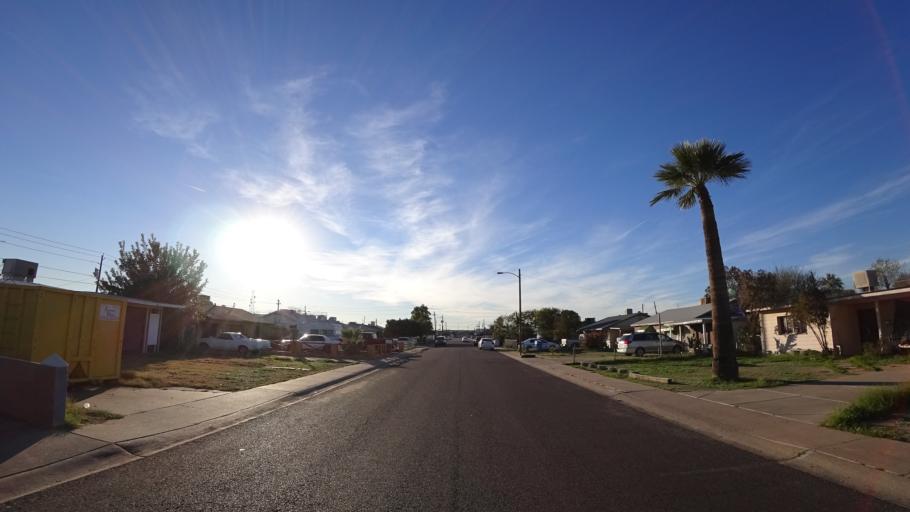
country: US
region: Arizona
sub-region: Maricopa County
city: Phoenix
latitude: 33.4710
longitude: -112.1031
